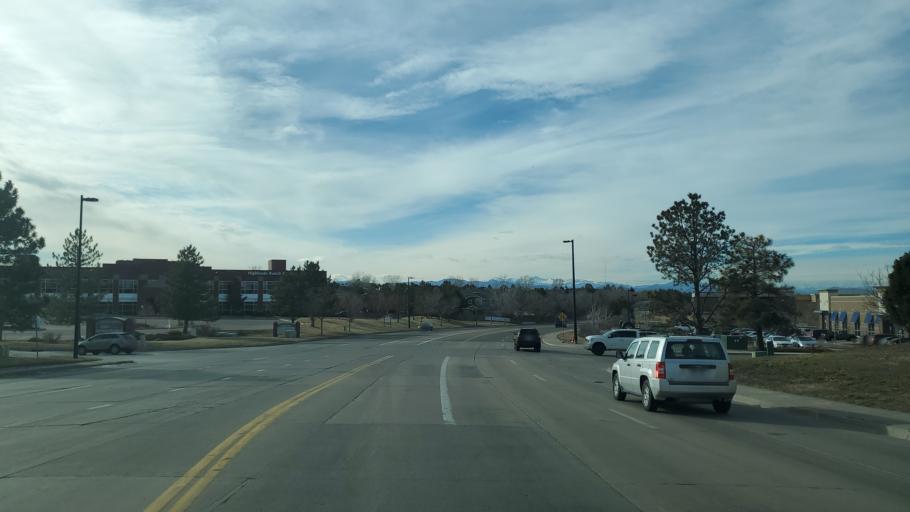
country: US
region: Colorado
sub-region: Douglas County
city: Acres Green
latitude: 39.5605
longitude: -104.9064
